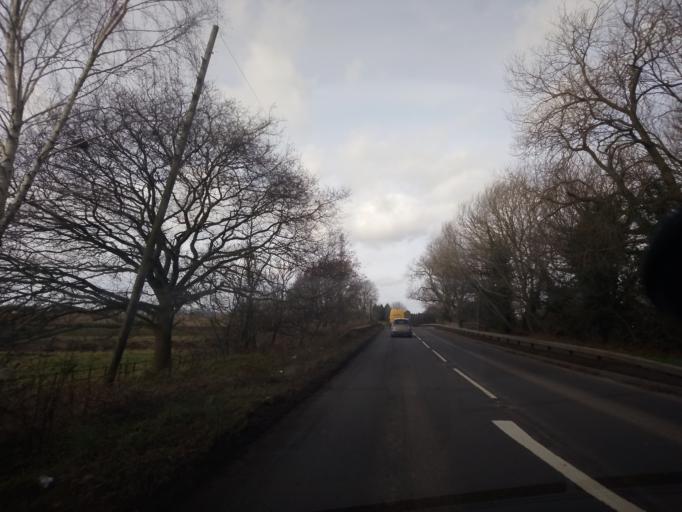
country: GB
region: England
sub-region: Telford and Wrekin
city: Eyton upon the Weald Moors
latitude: 52.7708
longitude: -2.5481
